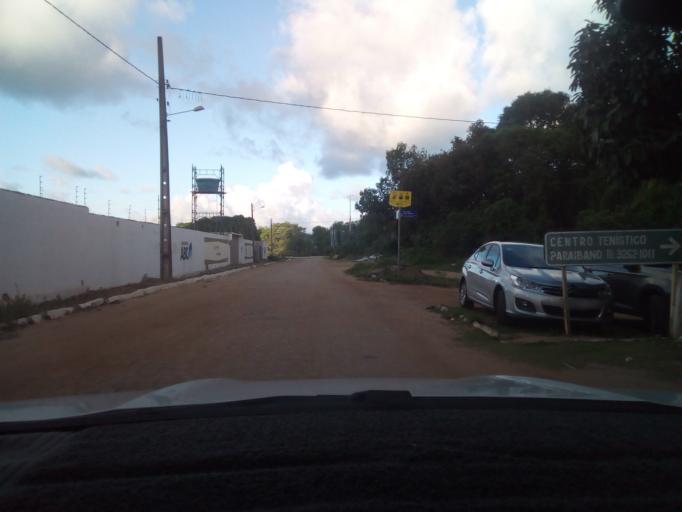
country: BR
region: Paraiba
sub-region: Joao Pessoa
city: Joao Pessoa
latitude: -7.1318
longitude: -34.8262
